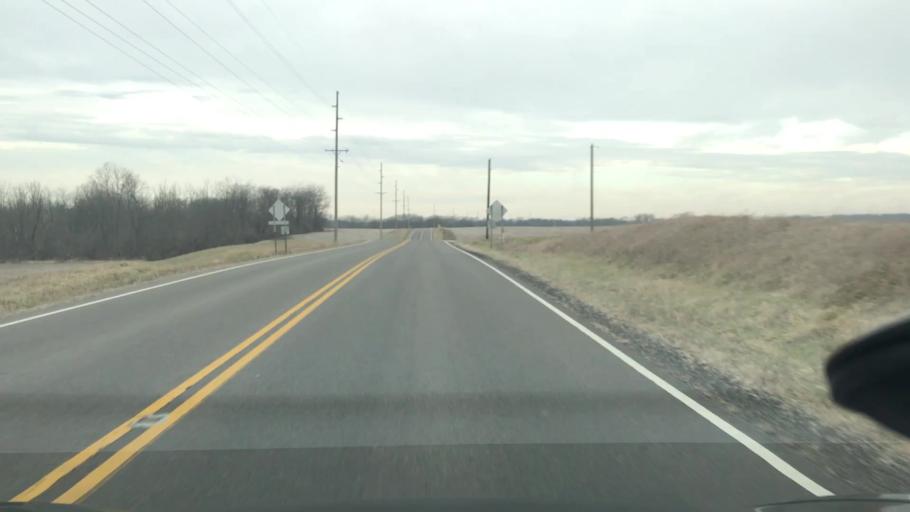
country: US
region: Ohio
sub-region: Madison County
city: London
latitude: 39.8556
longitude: -83.3982
